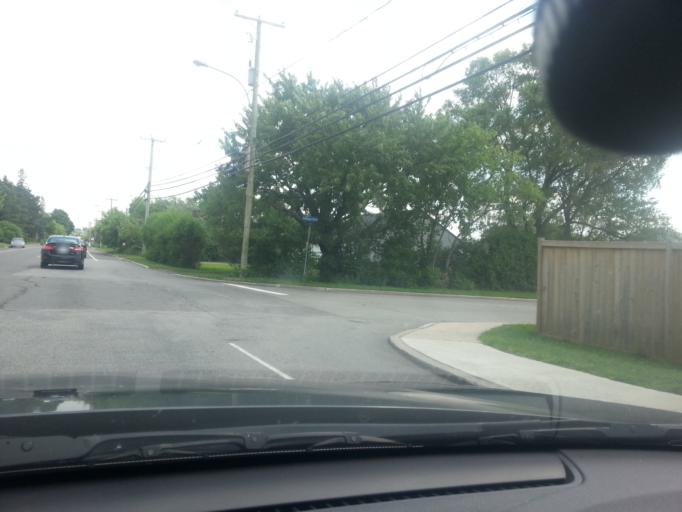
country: CA
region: Ontario
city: Bells Corners
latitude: 45.4064
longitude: -75.8633
